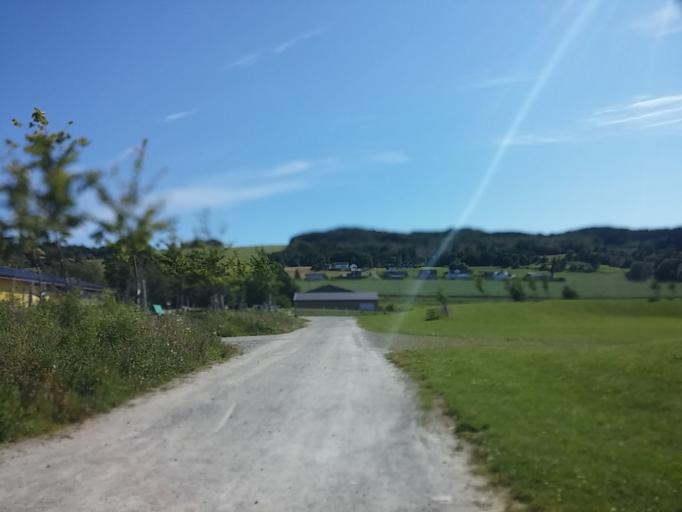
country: NO
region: Sor-Trondelag
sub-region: Malvik
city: Malvik
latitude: 63.4332
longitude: 10.7274
